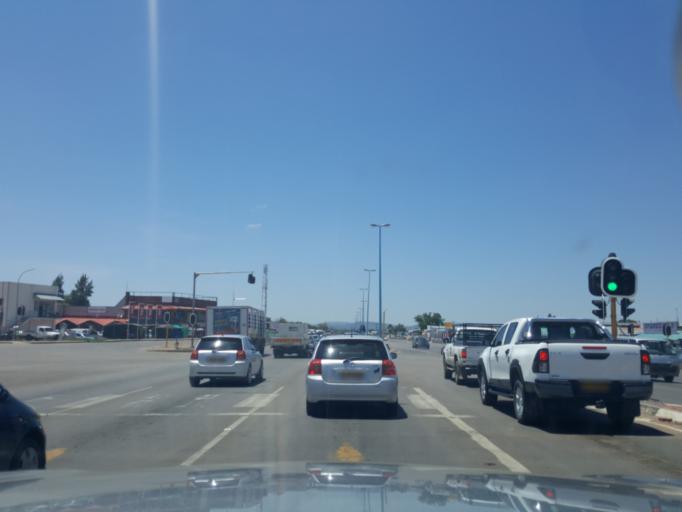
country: BW
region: Kweneng
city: Mogoditshane
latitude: -24.6215
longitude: 25.8671
